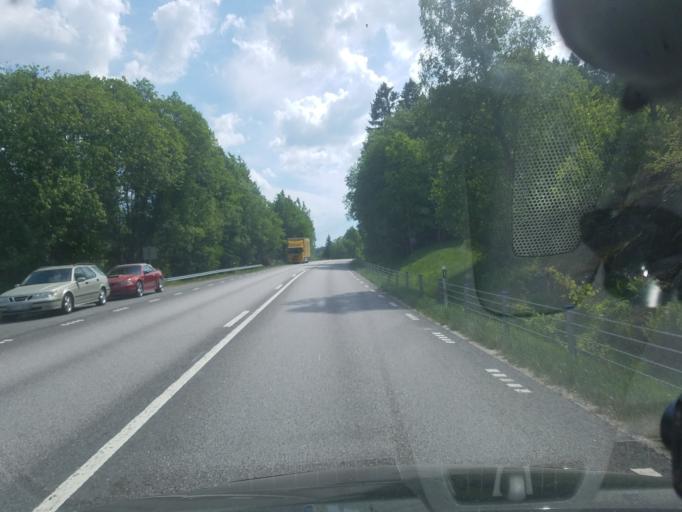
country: SE
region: Vaestra Goetaland
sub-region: Orust
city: Henan
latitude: 58.2163
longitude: 11.6907
